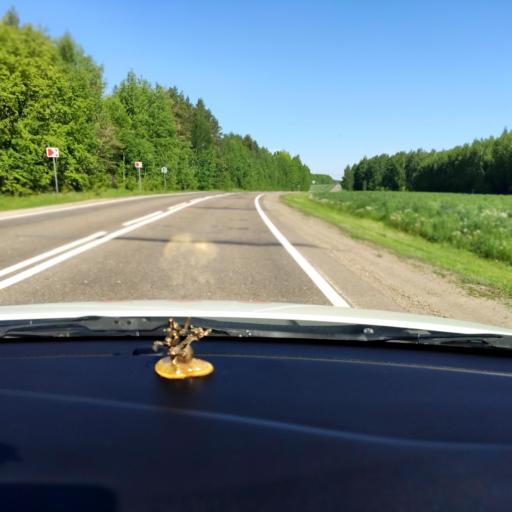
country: RU
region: Tatarstan
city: Vysokaya Gora
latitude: 56.0715
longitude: 49.1926
